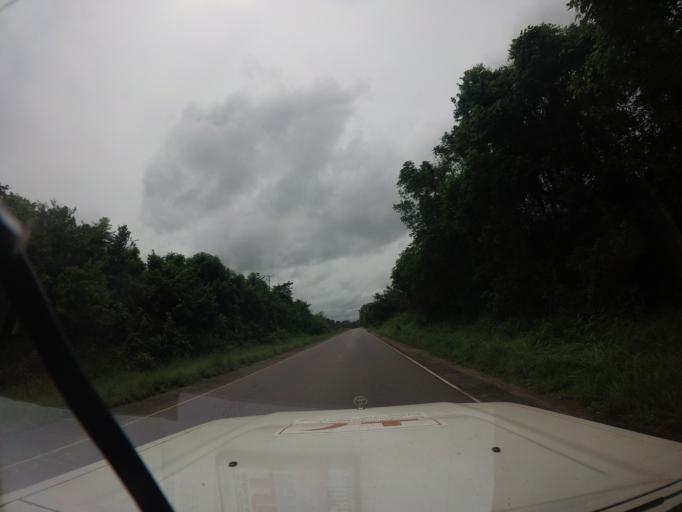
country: SL
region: Northern Province
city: Magburaka
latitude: 8.7454
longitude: -11.9628
